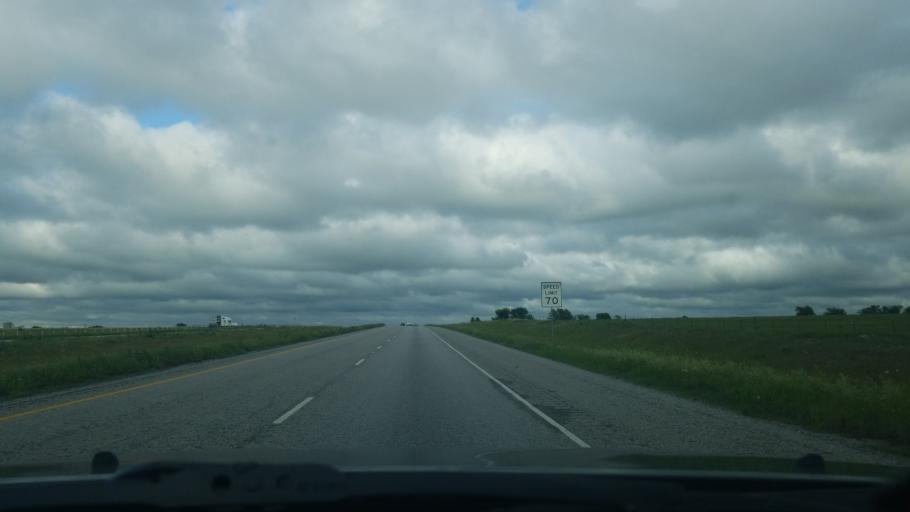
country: US
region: Texas
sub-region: Denton County
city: Ponder
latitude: 33.2395
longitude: -97.3402
